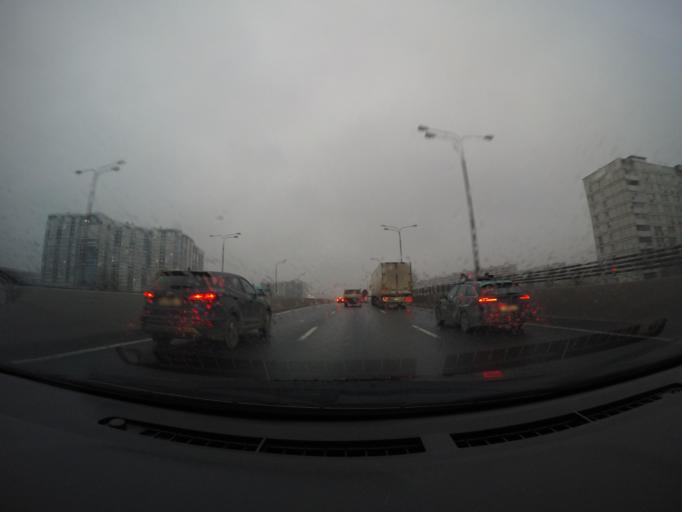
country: RU
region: Moscow
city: Chertanovo Yuzhnoye
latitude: 55.5940
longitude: 37.6014
